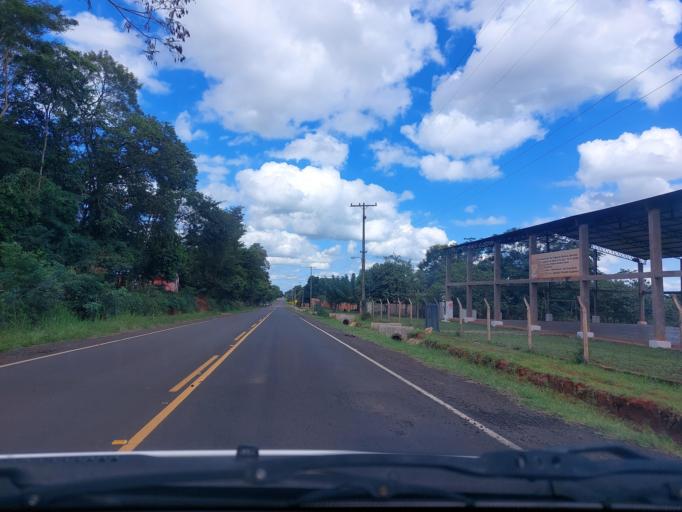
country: PY
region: San Pedro
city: Guayaybi
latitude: -24.5839
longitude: -56.5196
